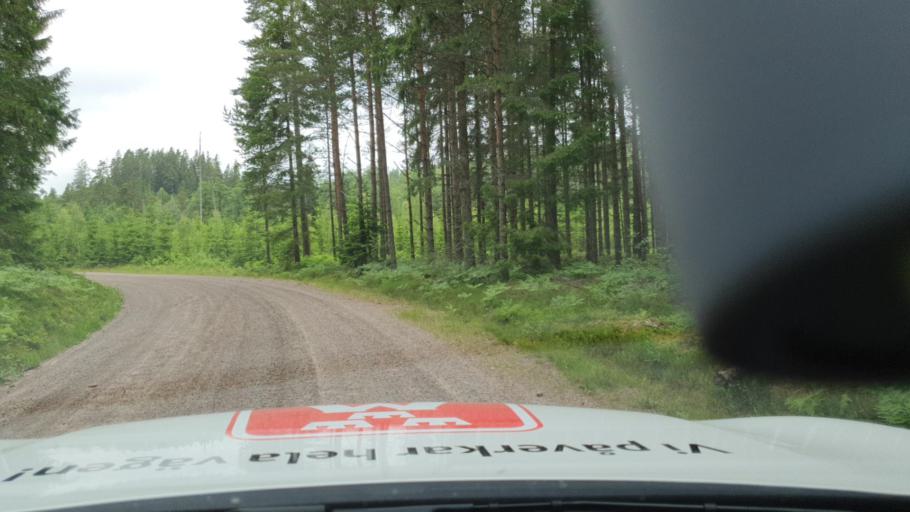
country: SE
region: Vaestra Goetaland
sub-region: Hjo Kommun
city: Hjo
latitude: 58.4068
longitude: 14.3297
